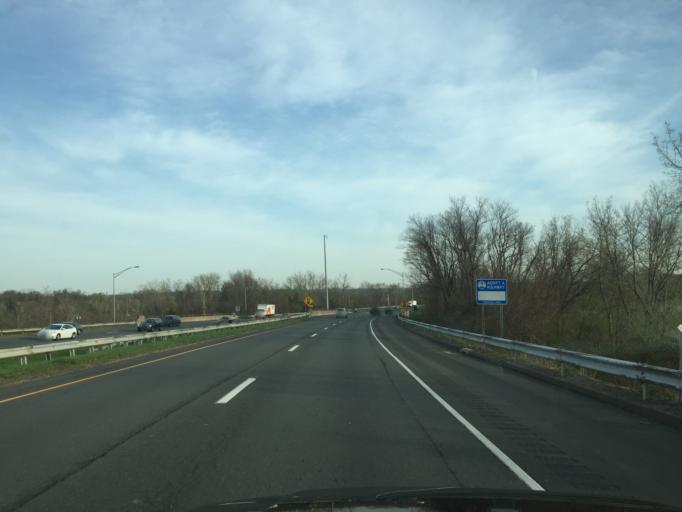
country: US
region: Connecticut
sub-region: Middlesex County
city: Cromwell
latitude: 41.5862
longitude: -72.6489
